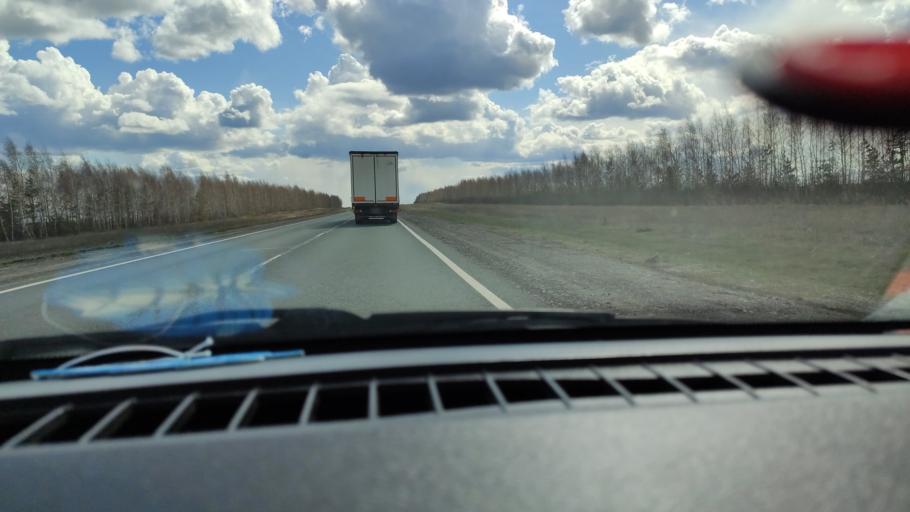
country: RU
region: Saratov
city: Dukhovnitskoye
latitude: 52.8151
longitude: 48.2312
